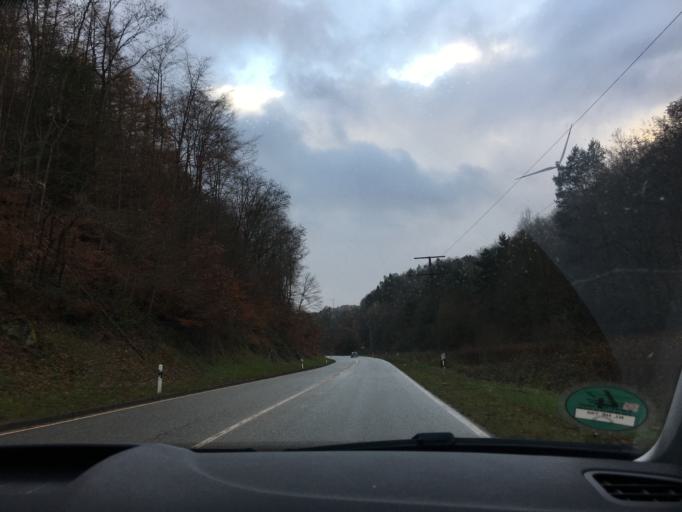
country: DE
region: Rheinland-Pfalz
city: Donsieders
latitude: 49.2503
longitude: 7.6031
